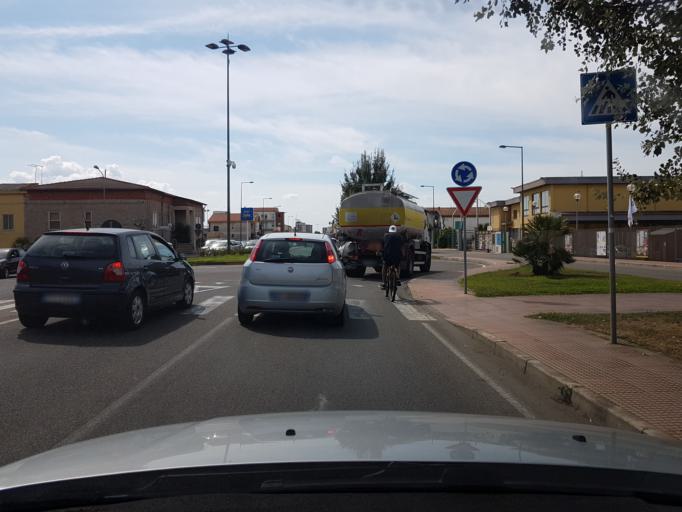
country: IT
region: Sardinia
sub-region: Provincia di Oristano
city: Oristano
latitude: 39.9150
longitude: 8.5855
